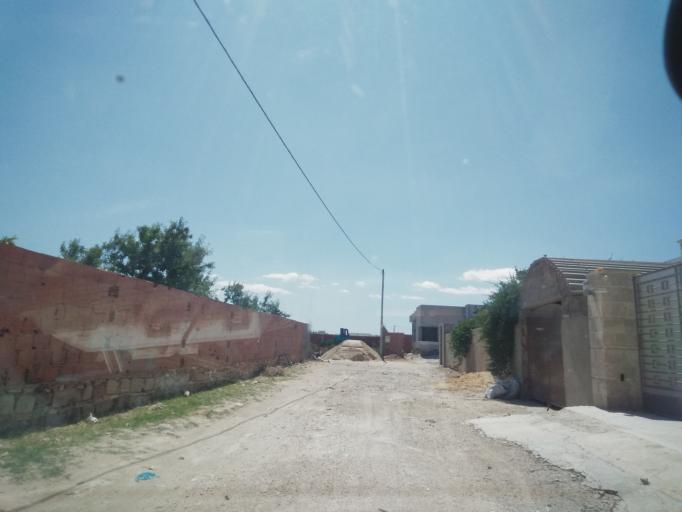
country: TN
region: Safaqis
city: Al Qarmadah
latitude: 34.8256
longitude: 10.7654
